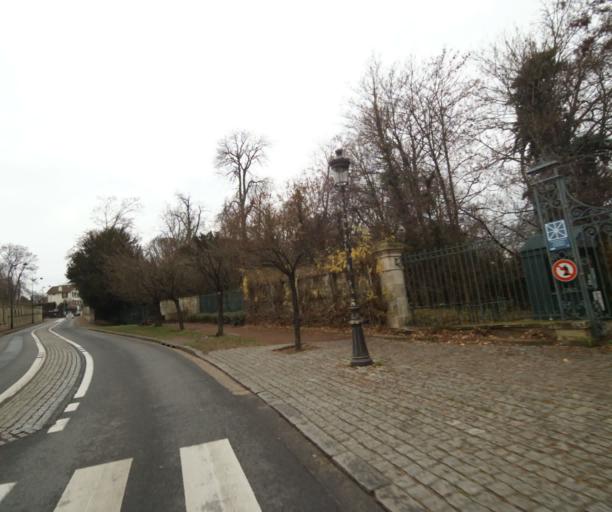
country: FR
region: Ile-de-France
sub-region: Departement des Hauts-de-Seine
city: Rueil-Malmaison
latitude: 48.8705
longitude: 2.1738
